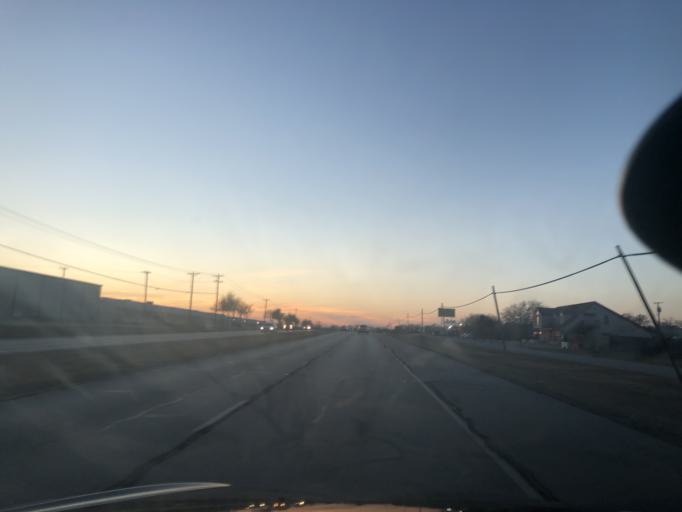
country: US
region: Texas
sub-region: Tarrant County
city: White Settlement
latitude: 32.7248
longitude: -97.4875
